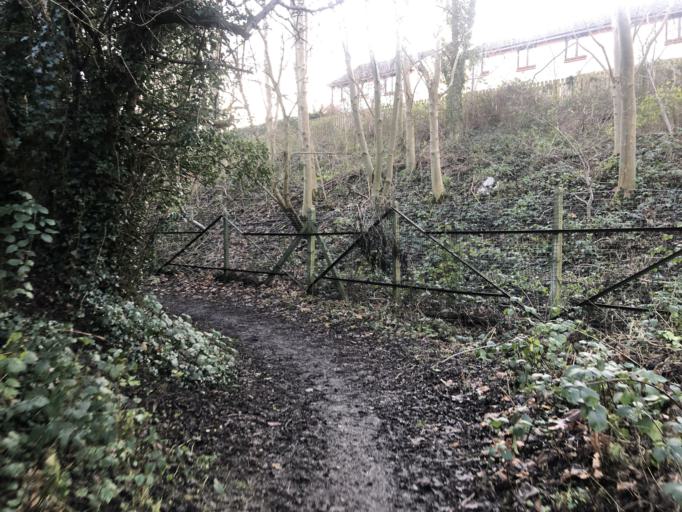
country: GB
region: Scotland
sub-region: Midlothian
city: Loanhead
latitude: 55.9090
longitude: -3.1468
